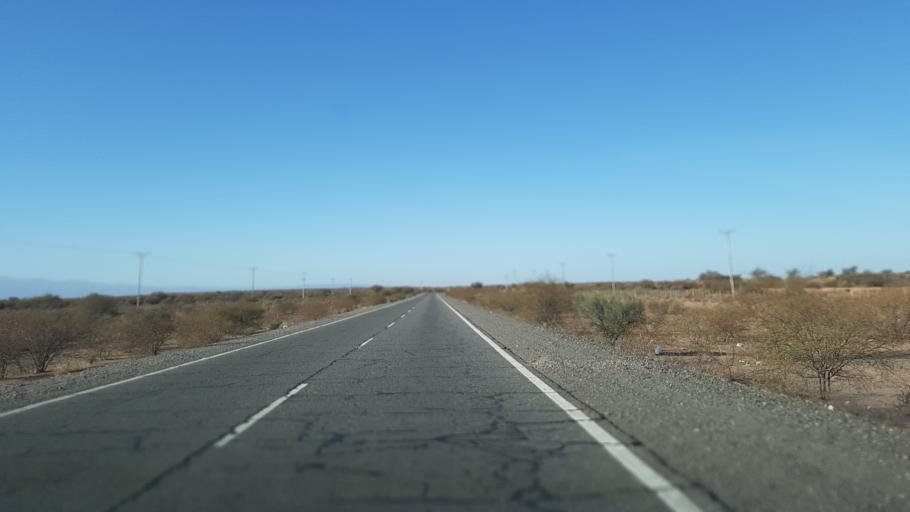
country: AR
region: San Juan
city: Caucete
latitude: -31.5998
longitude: -67.6992
